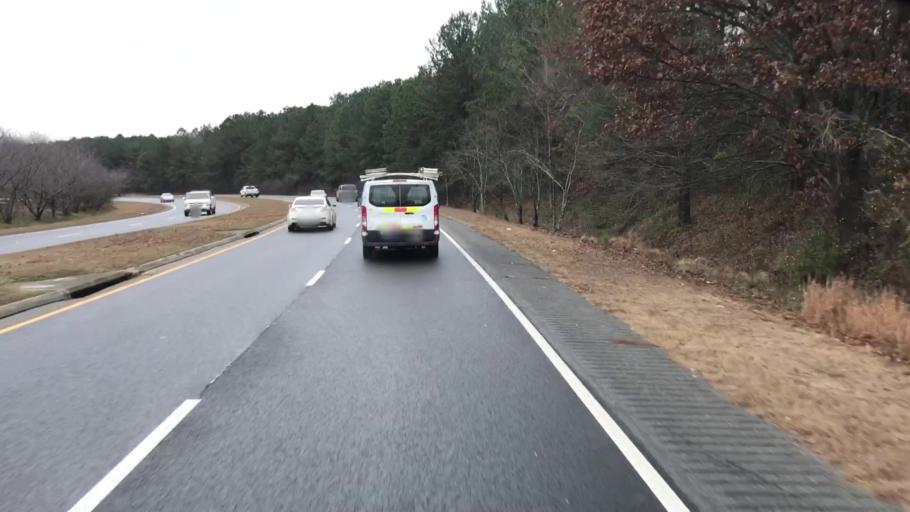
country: US
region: Georgia
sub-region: Gwinnett County
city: Snellville
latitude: 33.8763
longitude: -84.0243
